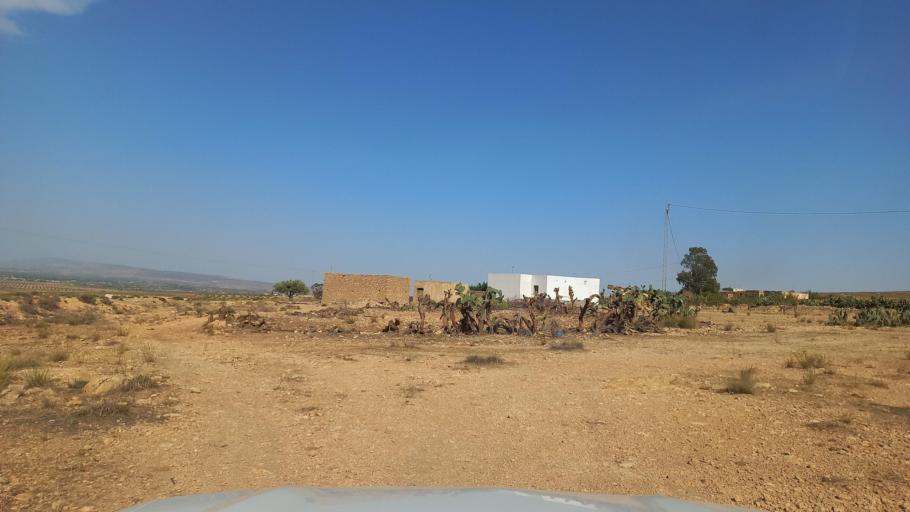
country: TN
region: Al Qasrayn
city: Kasserine
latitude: 35.2063
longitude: 8.9736
